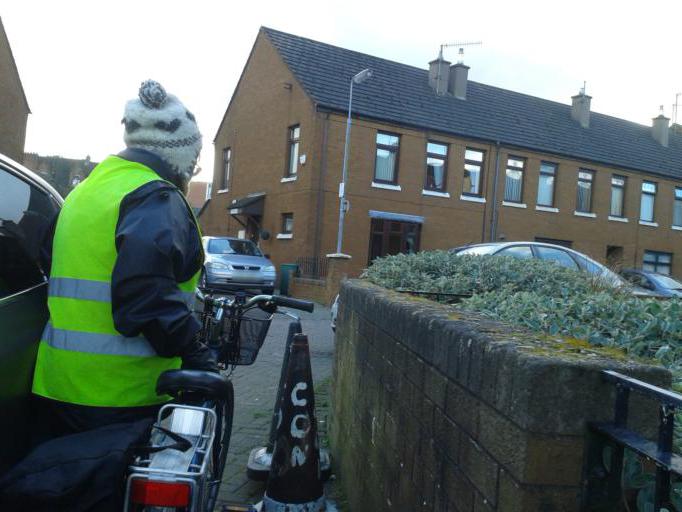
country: GB
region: Northern Ireland
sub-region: City of Belfast
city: Belfast
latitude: 54.5944
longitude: -5.9251
